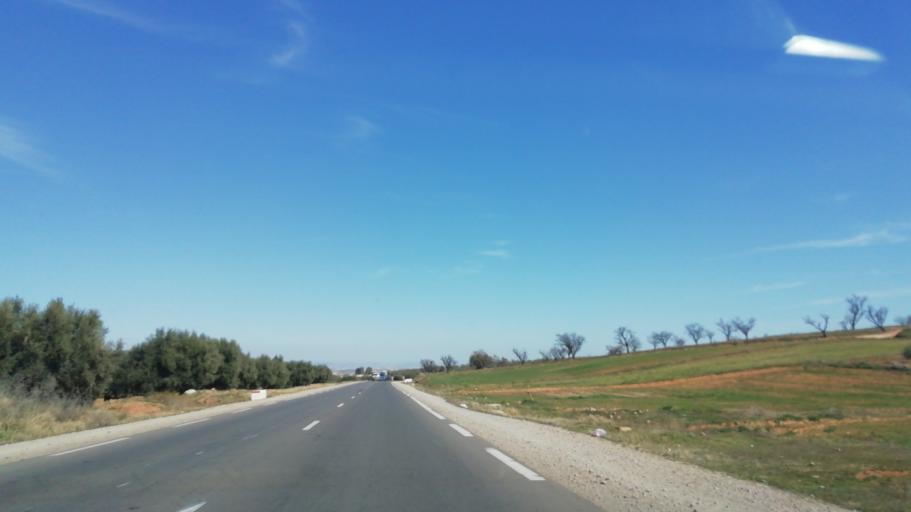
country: DZ
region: Mascara
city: Oued el Abtal
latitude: 35.4267
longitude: 0.4646
